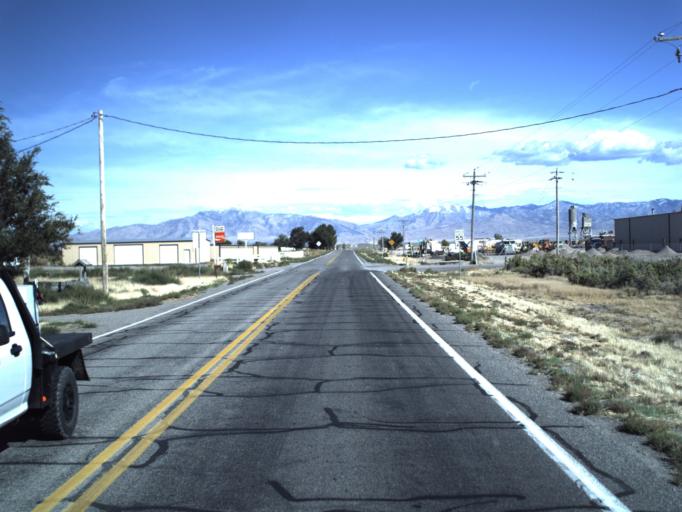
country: US
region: Utah
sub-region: Millard County
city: Delta
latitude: 39.3527
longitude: -112.5490
